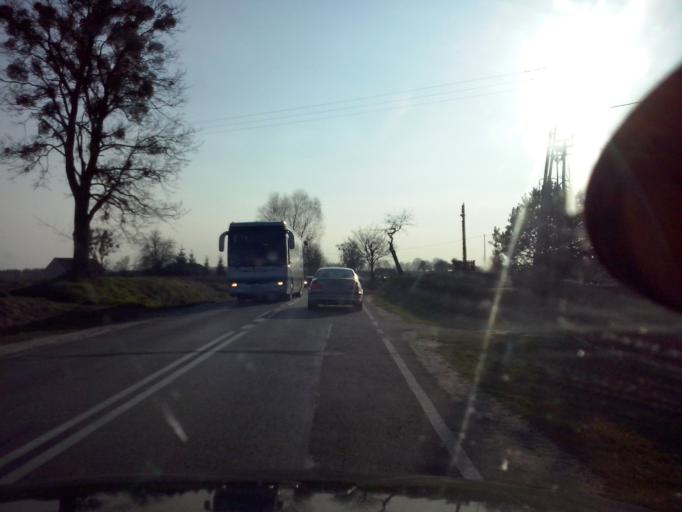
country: PL
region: Lublin Voivodeship
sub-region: Powiat janowski
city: Modliborzyce
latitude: 50.7544
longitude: 22.2776
